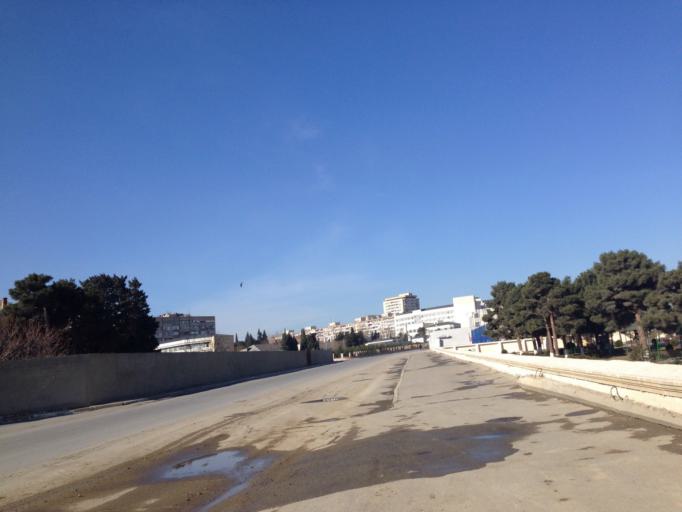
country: AZ
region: Baki
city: Baku
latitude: 40.4102
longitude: 49.8543
